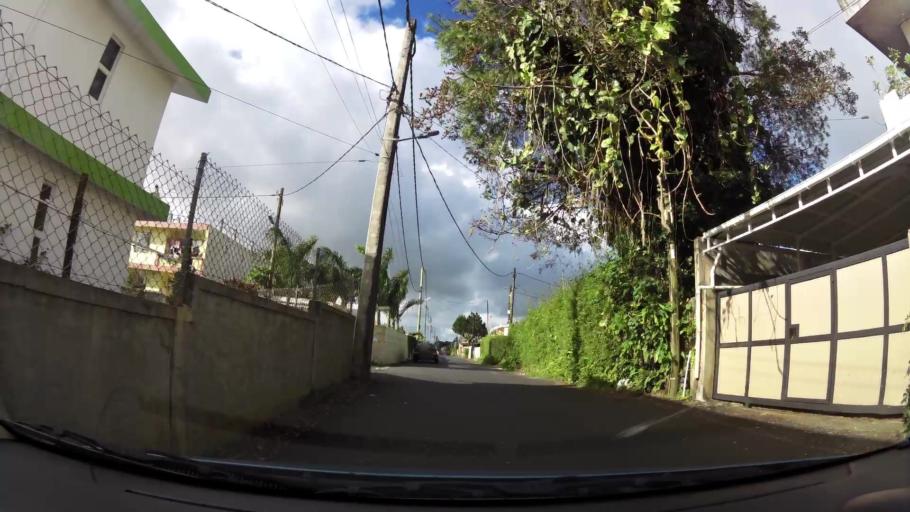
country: MU
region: Plaines Wilhems
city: Curepipe
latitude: -20.3274
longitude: 57.5205
